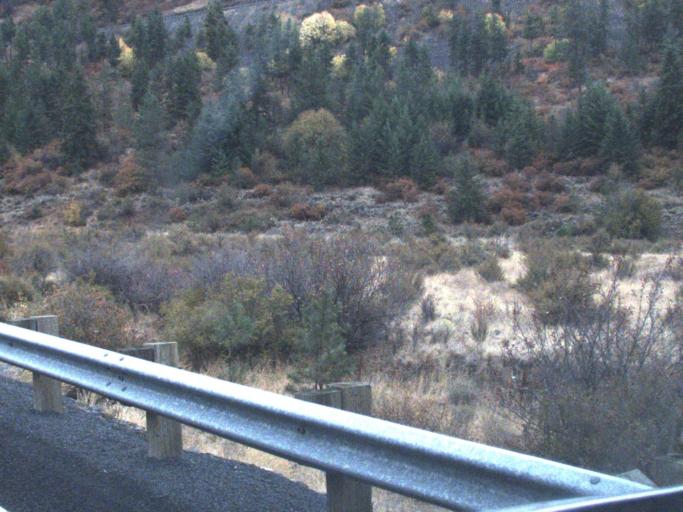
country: US
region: Washington
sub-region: Okanogan County
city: Coulee Dam
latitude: 47.8769
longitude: -118.7161
